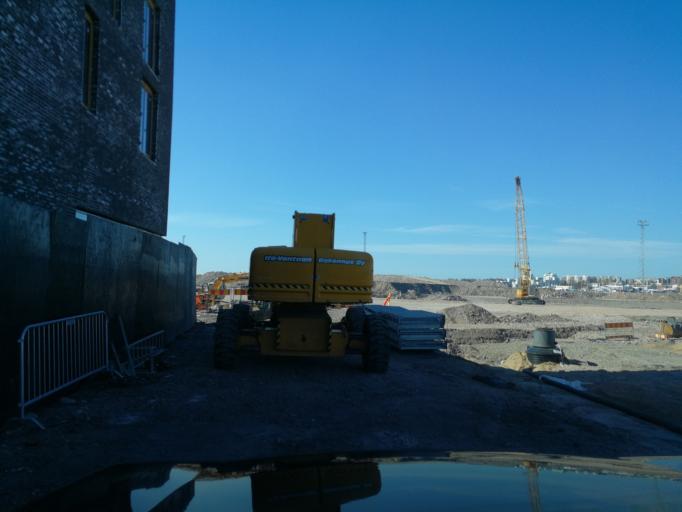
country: FI
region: Uusimaa
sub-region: Helsinki
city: Helsinki
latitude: 60.1557
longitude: 24.9089
